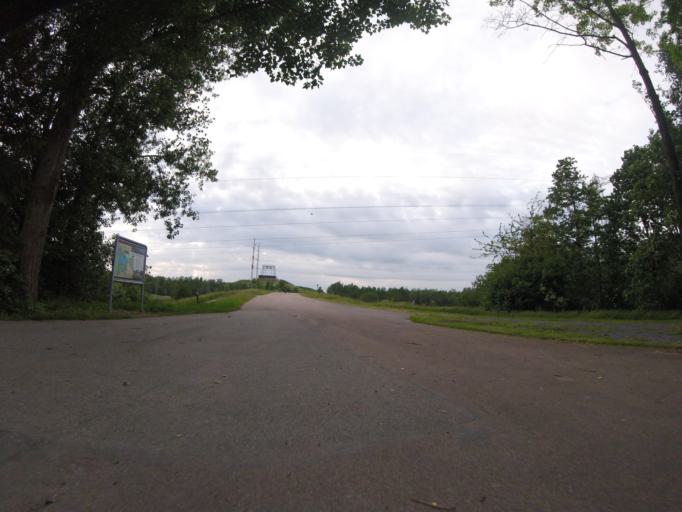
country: NL
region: North Holland
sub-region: Gemeente Haarlemmermeer
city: Hoofddorp
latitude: 52.3329
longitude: 4.6738
